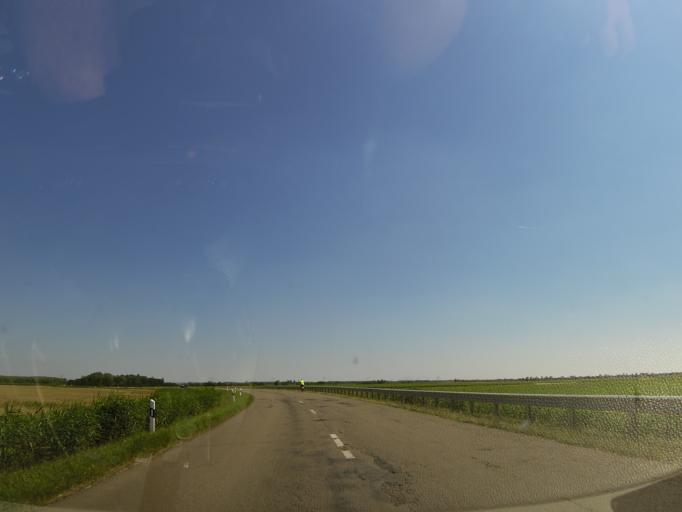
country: HU
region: Jasz-Nagykun-Szolnok
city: Fegyvernek
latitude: 47.2593
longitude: 20.5718
